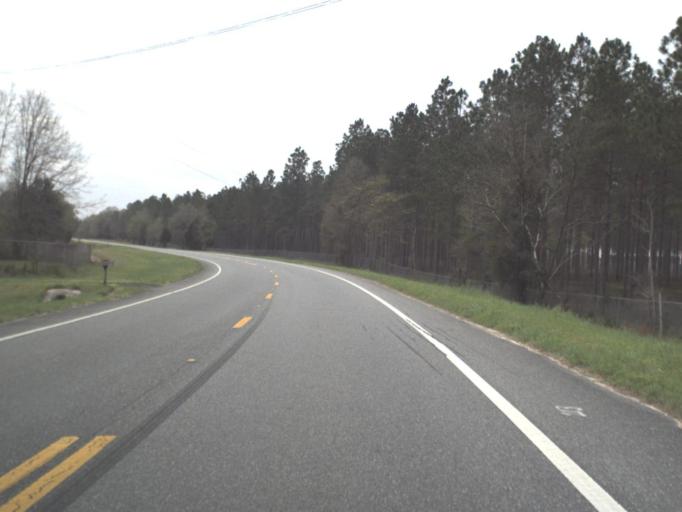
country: US
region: Florida
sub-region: Calhoun County
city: Blountstown
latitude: 30.5116
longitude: -85.2000
